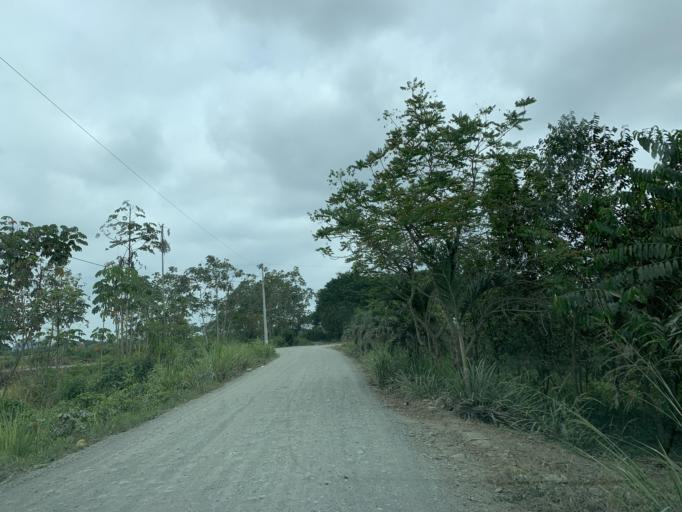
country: EC
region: Guayas
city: Coronel Marcelino Mariduena
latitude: -2.3202
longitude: -79.4705
